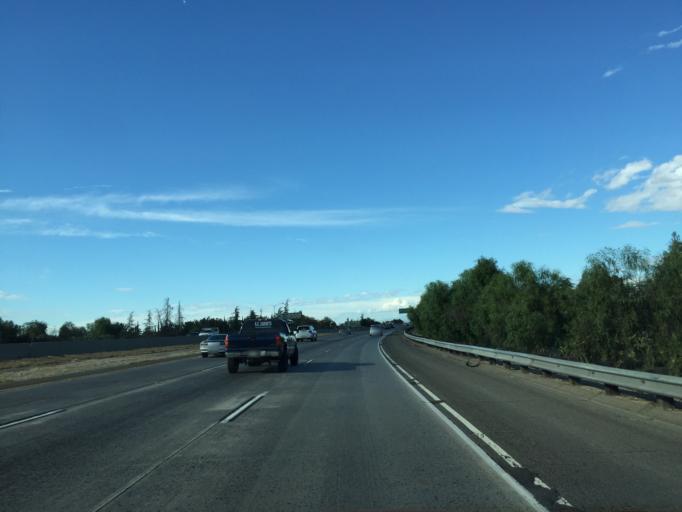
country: US
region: California
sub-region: Fresno County
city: Fresno
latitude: 36.7733
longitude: -119.7848
